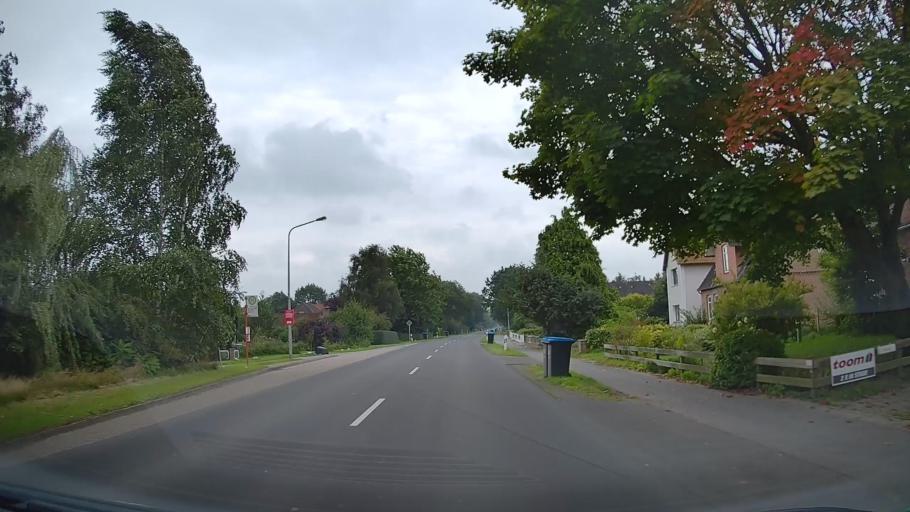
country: DE
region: Lower Saxony
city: Drochtersen
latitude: 53.7320
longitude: 9.3497
